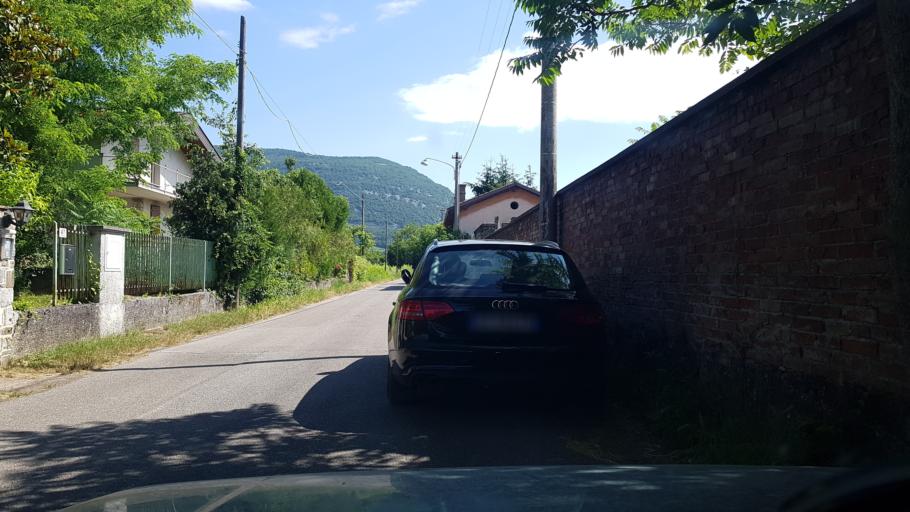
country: IT
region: Friuli Venezia Giulia
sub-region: Provincia di Gorizia
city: Gorizia
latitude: 45.9628
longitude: 13.6243
